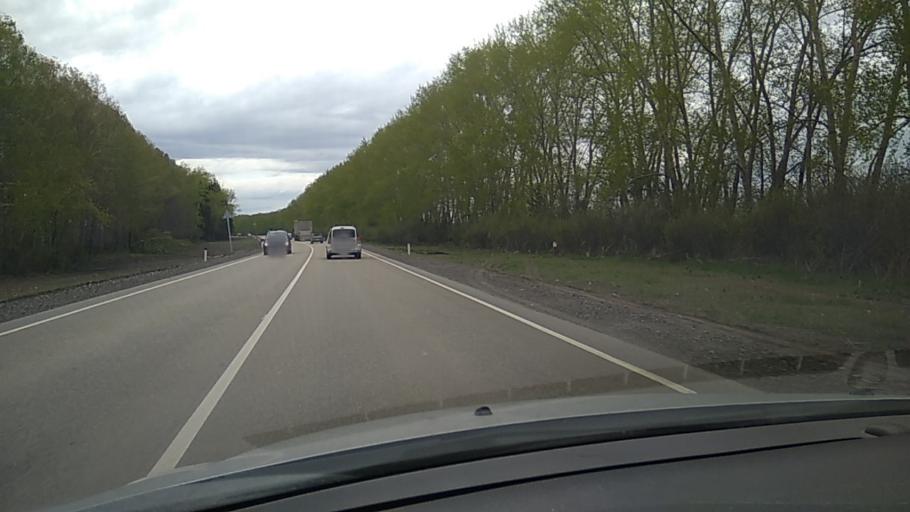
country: RU
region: Sverdlovsk
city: Dvurechensk
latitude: 56.6448
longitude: 61.2143
